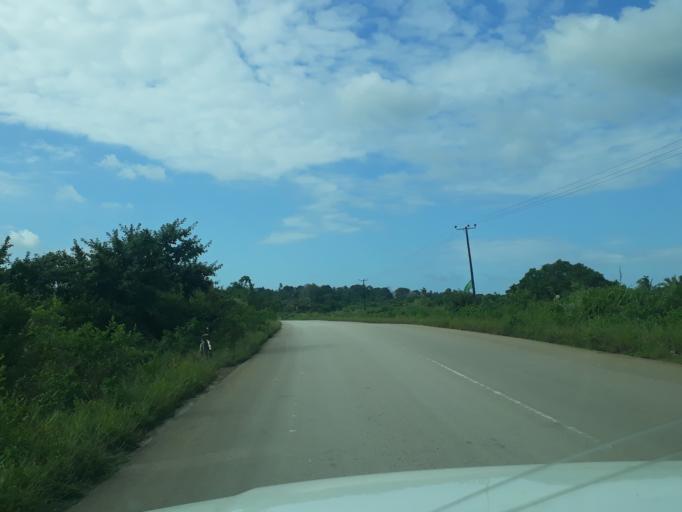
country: TZ
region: Zanzibar North
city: Kijini
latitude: -5.8368
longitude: 39.2883
